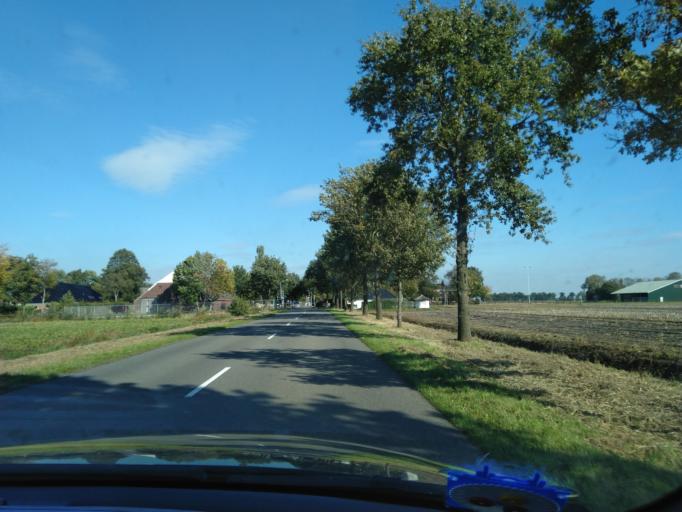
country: NL
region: Groningen
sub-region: Gemeente Hoogezand-Sappemeer
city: Sappemeer
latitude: 53.0882
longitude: 6.7944
